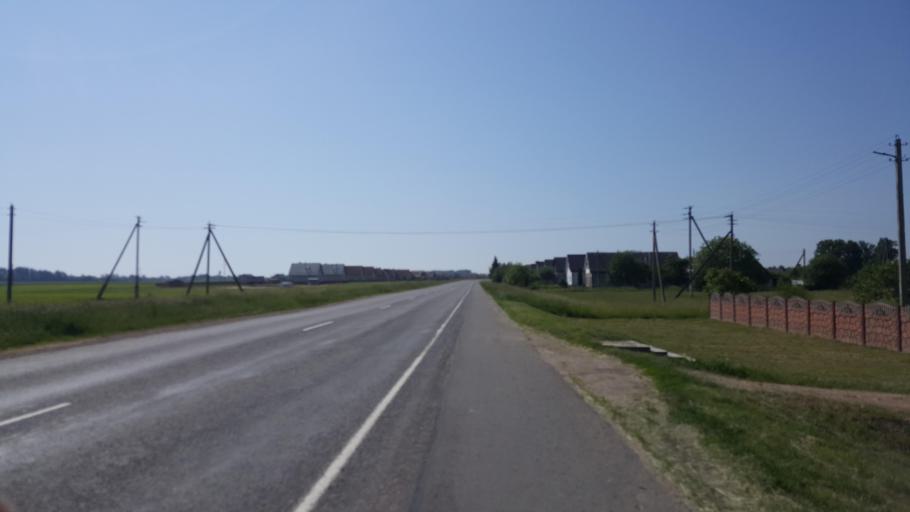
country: BY
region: Brest
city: Kamyanyets
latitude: 52.3308
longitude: 23.9142
